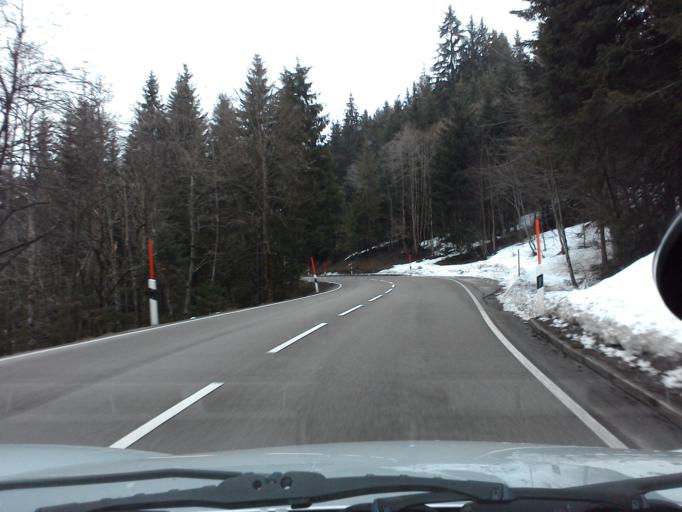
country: DE
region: Bavaria
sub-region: Swabia
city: Oberstdorf
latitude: 47.3943
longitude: 10.2359
